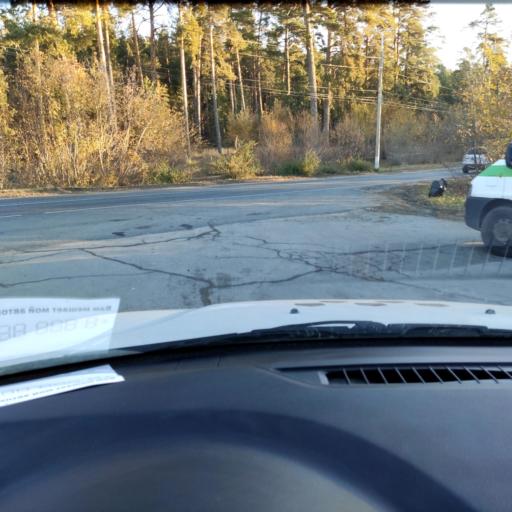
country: RU
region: Samara
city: Tol'yatti
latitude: 53.4761
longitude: 49.3270
